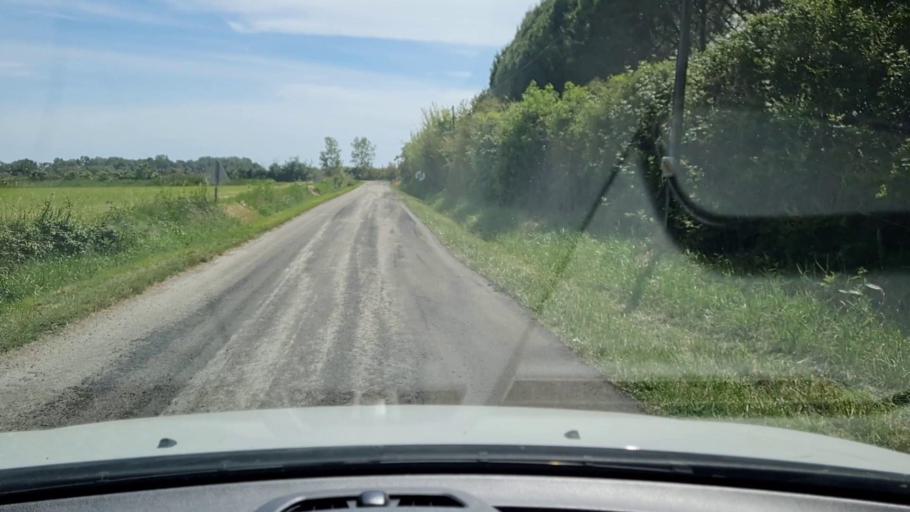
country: FR
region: Provence-Alpes-Cote d'Azur
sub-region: Departement des Bouches-du-Rhone
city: Saintes-Maries-de-la-Mer
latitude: 43.5628
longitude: 4.3827
